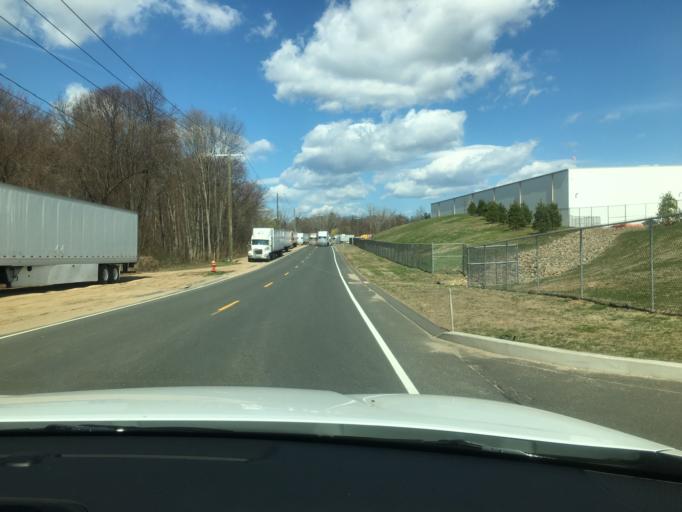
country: US
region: Connecticut
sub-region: Hartford County
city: Blue Hills
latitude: 41.8676
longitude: -72.7096
